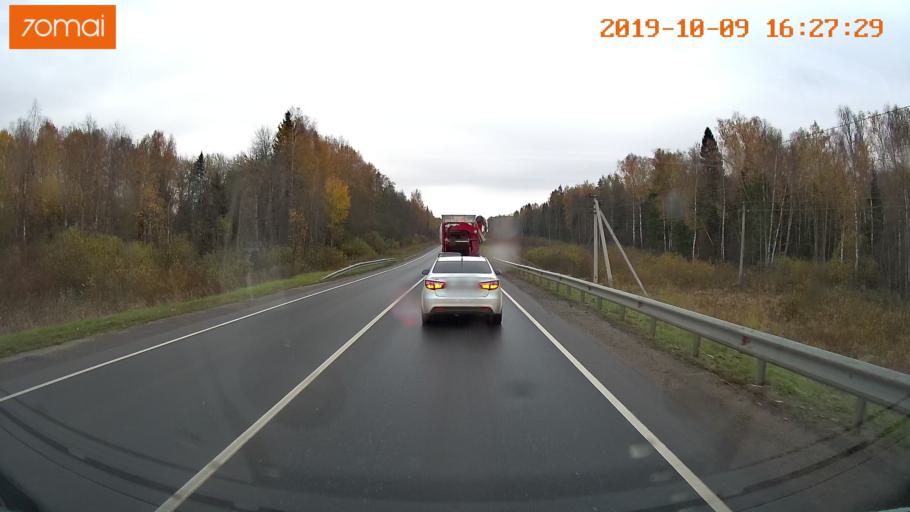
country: RU
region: Kostroma
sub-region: Kostromskoy Rayon
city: Kostroma
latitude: 57.6331
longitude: 40.9282
